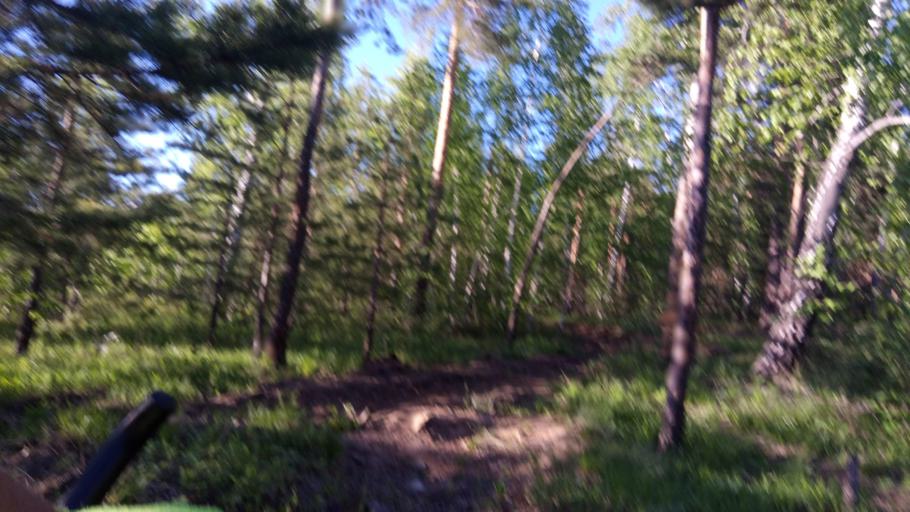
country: RU
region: Chelyabinsk
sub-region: Gorod Chelyabinsk
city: Chelyabinsk
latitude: 55.1248
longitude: 61.3435
